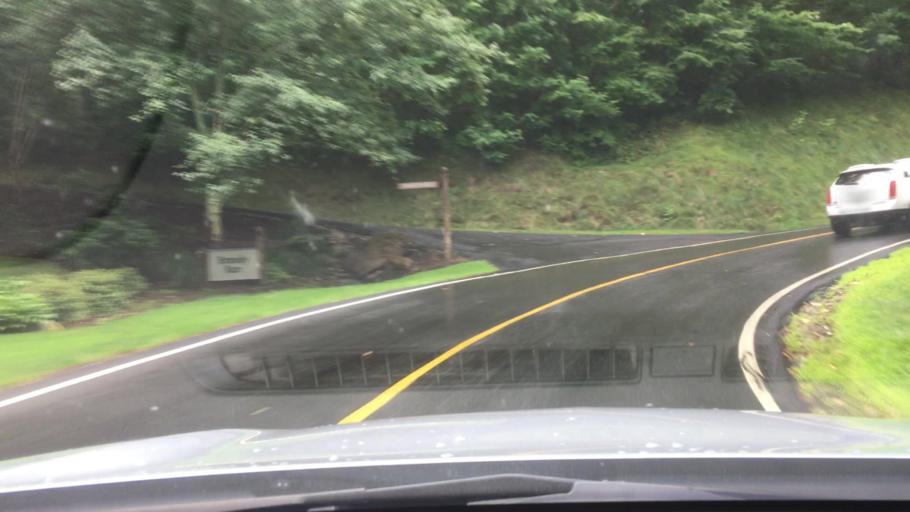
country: US
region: North Carolina
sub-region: Yancey County
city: Burnsville
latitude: 35.8769
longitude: -82.3481
